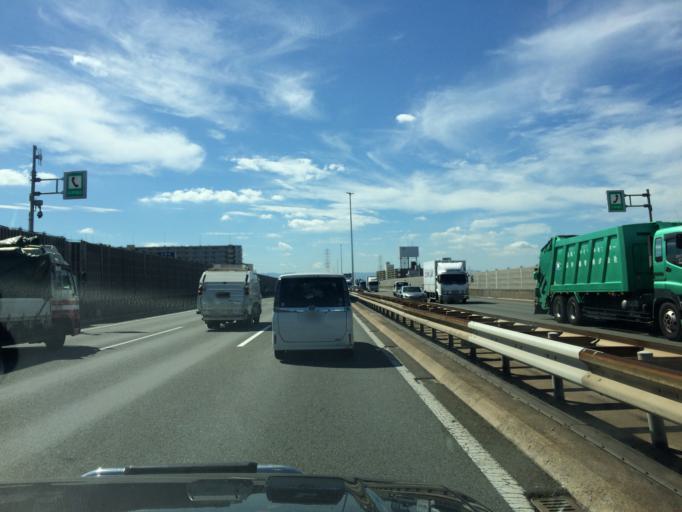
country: JP
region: Osaka
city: Yao
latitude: 34.6118
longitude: 135.5742
